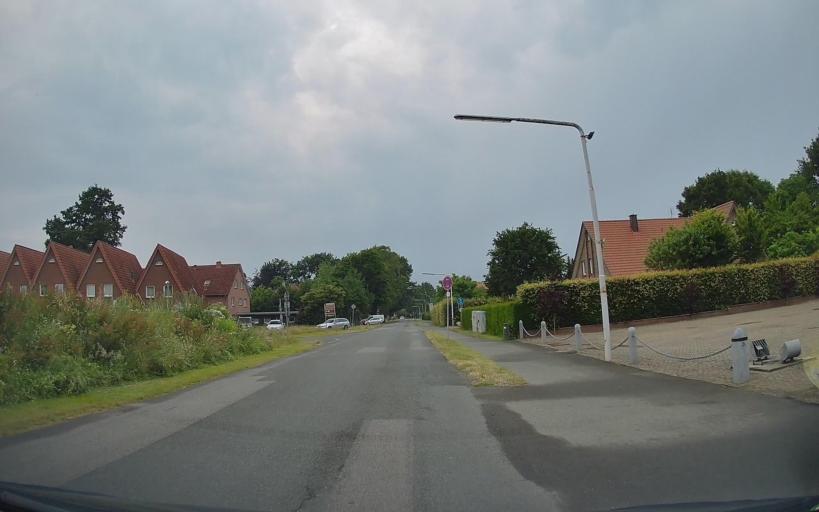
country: DE
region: Lower Saxony
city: Friesoythe
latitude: 53.0147
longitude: 7.8599
